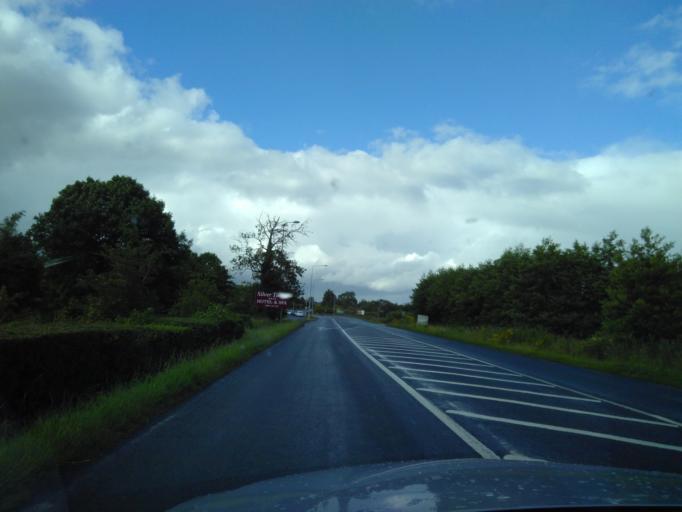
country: IE
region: Ulster
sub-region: County Donegal
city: Ramelton
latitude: 54.9842
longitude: -7.6720
